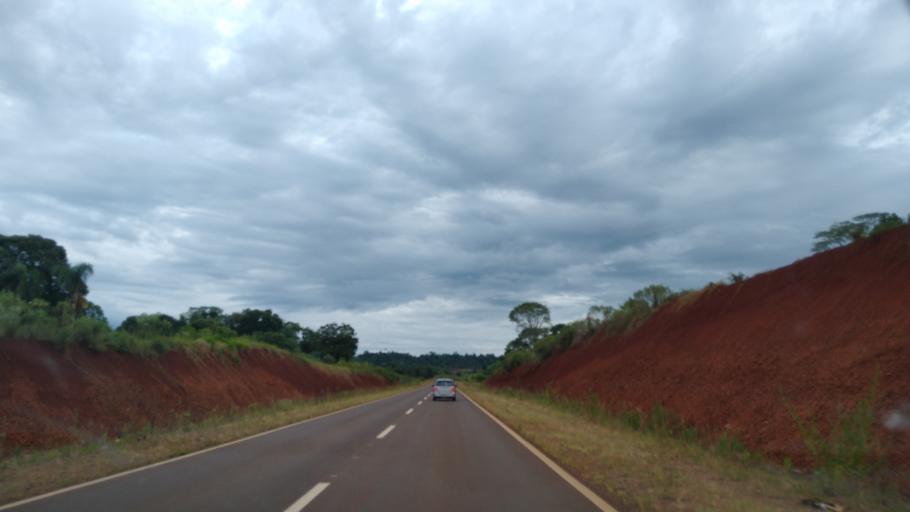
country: AR
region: Misiones
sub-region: Departamento de San Pedro
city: San Pedro
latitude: -26.4618
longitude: -53.8743
